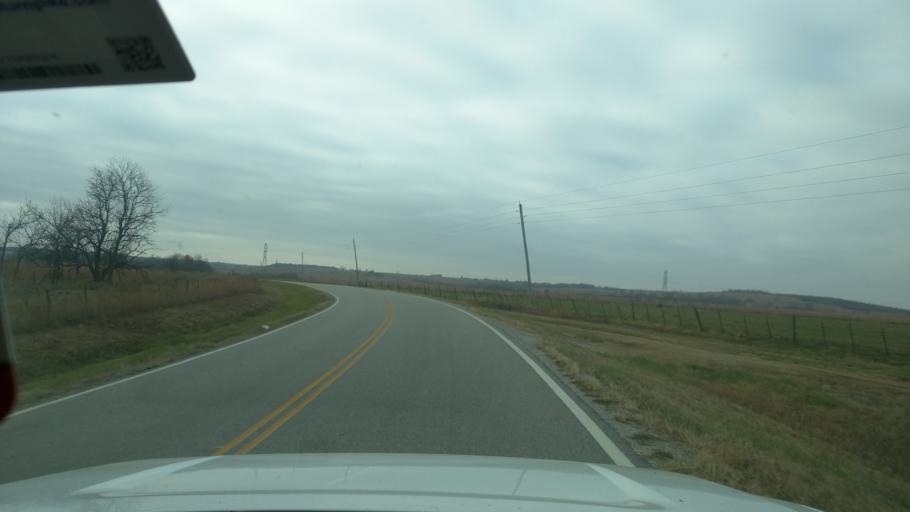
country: US
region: Kansas
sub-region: Greenwood County
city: Eureka
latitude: 37.6877
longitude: -96.2340
